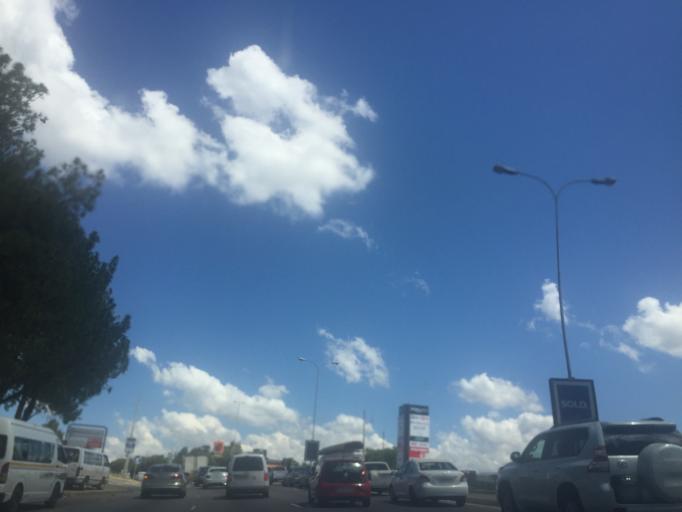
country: ZA
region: Gauteng
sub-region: City of Johannesburg Metropolitan Municipality
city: Diepsloot
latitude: -26.0417
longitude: 28.0150
